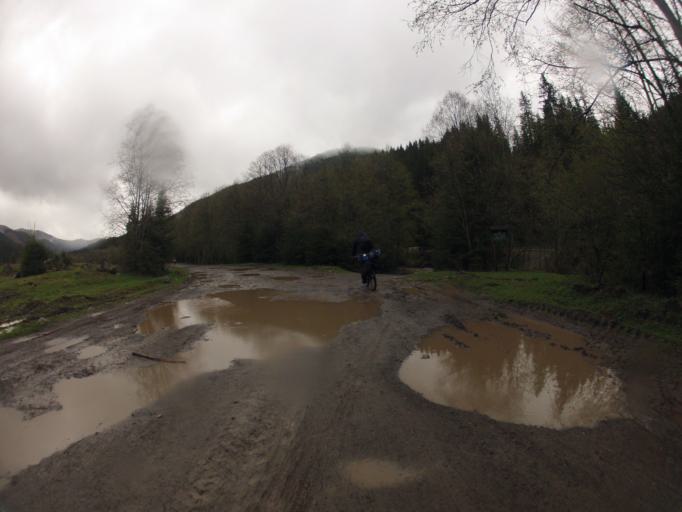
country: RO
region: Suceava
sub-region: Comuna Izvoarele Sucevei
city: Izvoarele Sucevei
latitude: 47.8333
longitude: 25.0565
